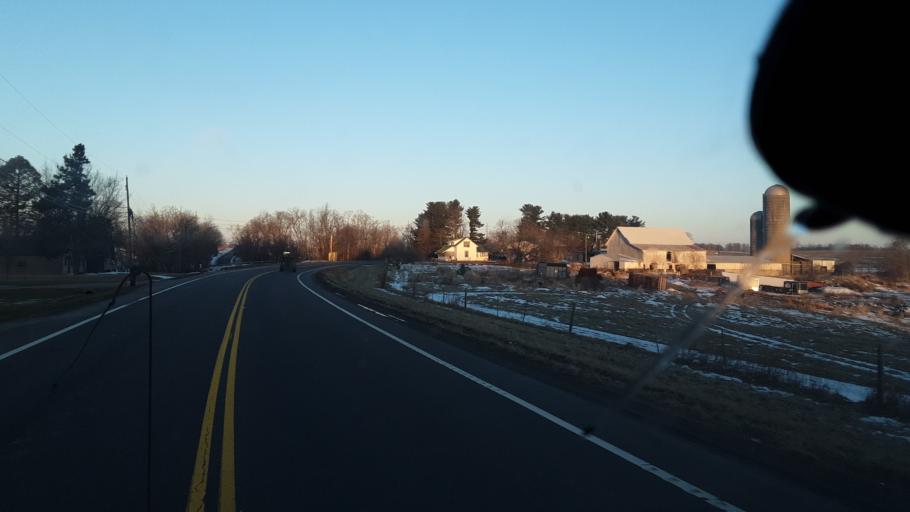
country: US
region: Ohio
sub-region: Perry County
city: Somerset
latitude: 39.8137
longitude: -82.3131
